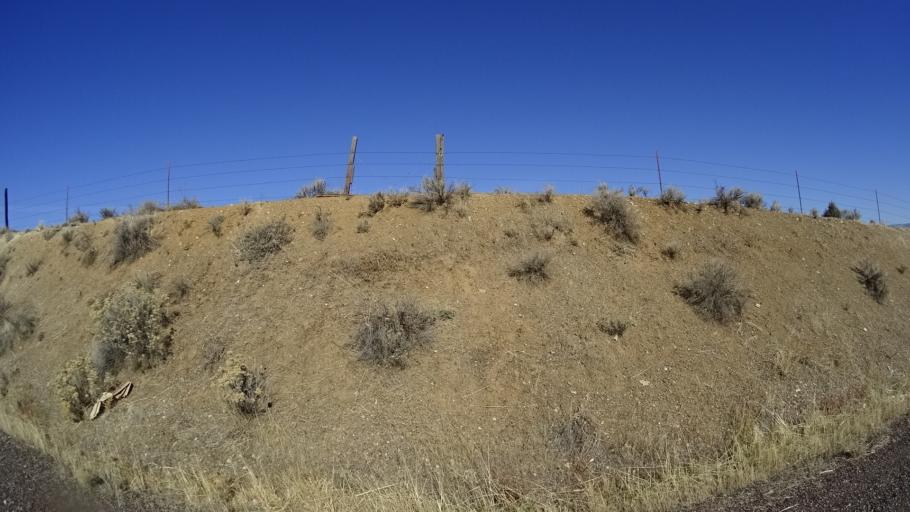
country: US
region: California
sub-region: Siskiyou County
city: Montague
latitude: 41.7456
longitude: -122.5797
